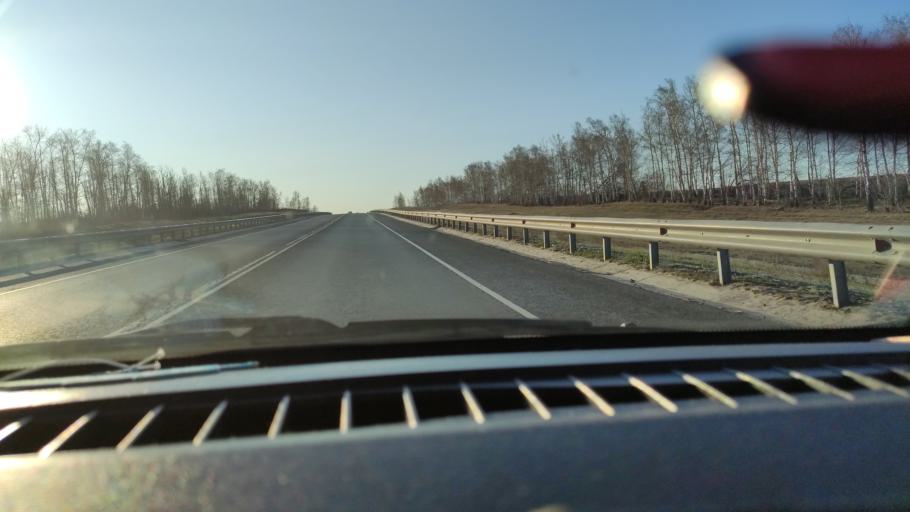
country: RU
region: Saratov
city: Shikhany
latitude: 52.1229
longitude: 47.2544
